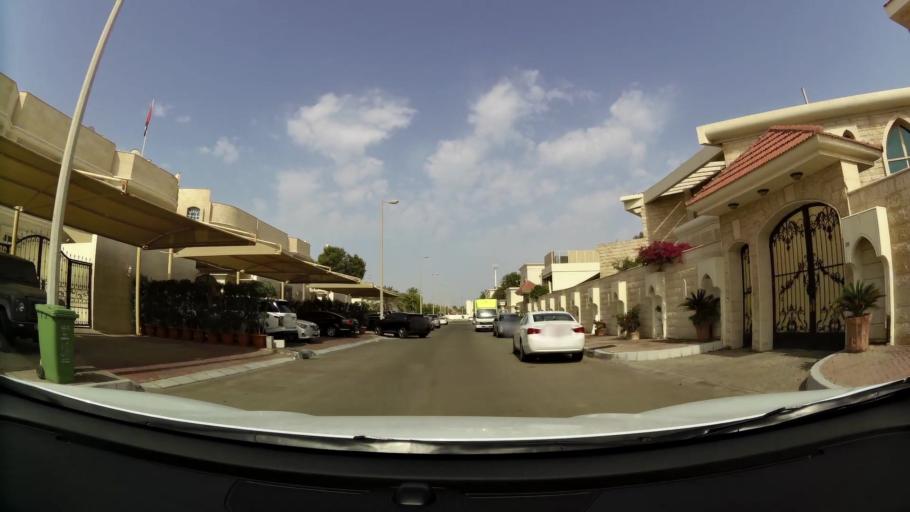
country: AE
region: Abu Dhabi
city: Abu Dhabi
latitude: 24.4434
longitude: 54.3600
